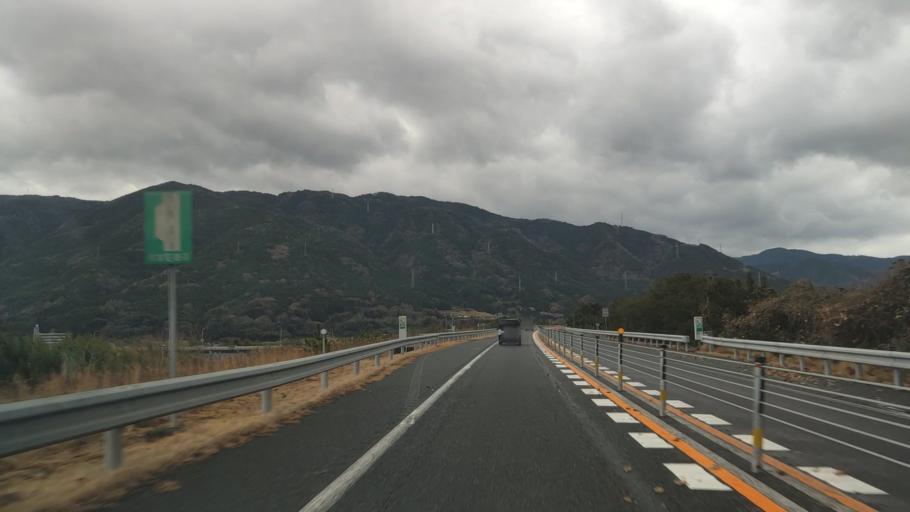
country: JP
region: Tokushima
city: Ikedacho
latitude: 34.0433
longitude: 133.9112
